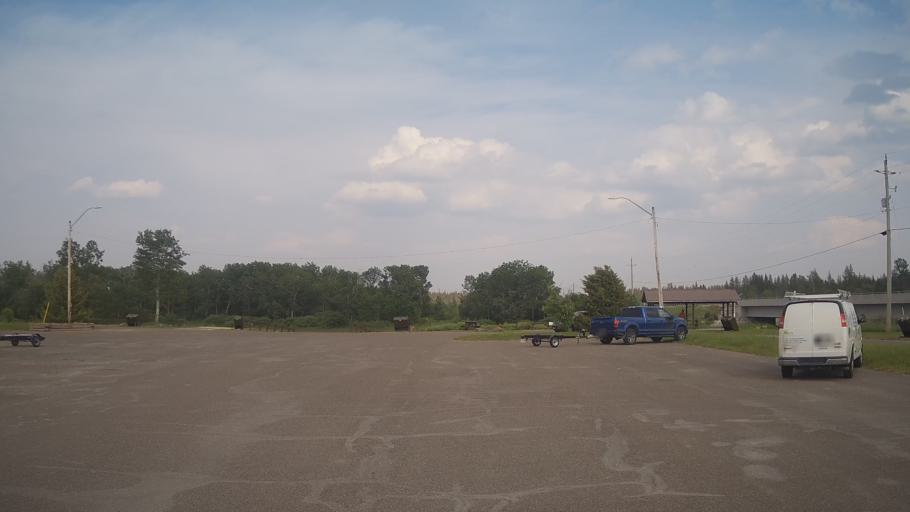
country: CA
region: Ontario
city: Kapuskasing
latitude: 49.5243
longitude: -82.8424
